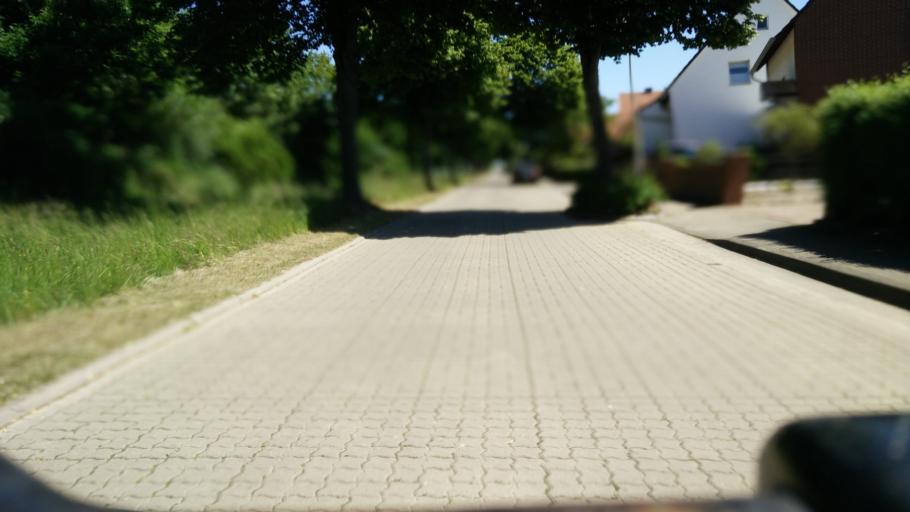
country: DE
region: Lower Saxony
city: Wunstorf
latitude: 52.3969
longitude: 9.4567
